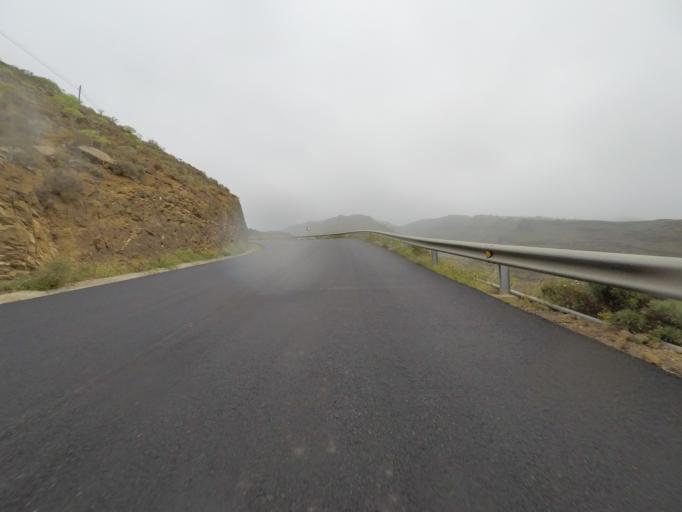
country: ES
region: Canary Islands
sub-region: Provincia de Santa Cruz de Tenerife
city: Alajero
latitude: 28.0564
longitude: -17.2016
